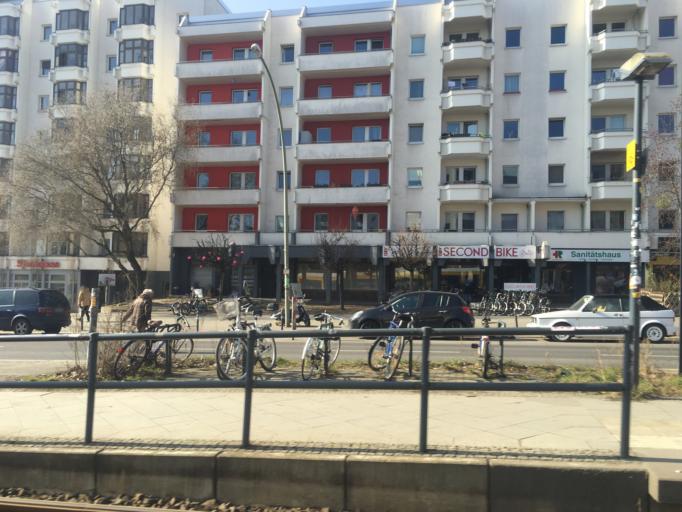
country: DE
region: Berlin
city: Friedrichshain Bezirk
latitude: 52.5191
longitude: 13.4525
